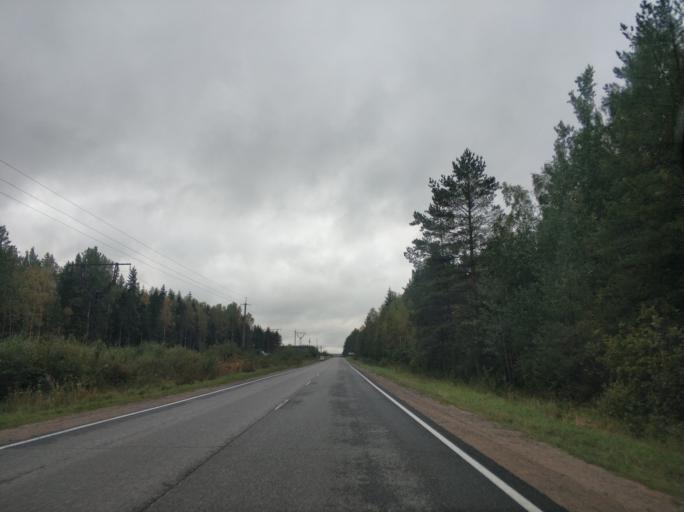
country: RU
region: Leningrad
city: Borisova Griva
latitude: 60.1019
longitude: 30.9565
